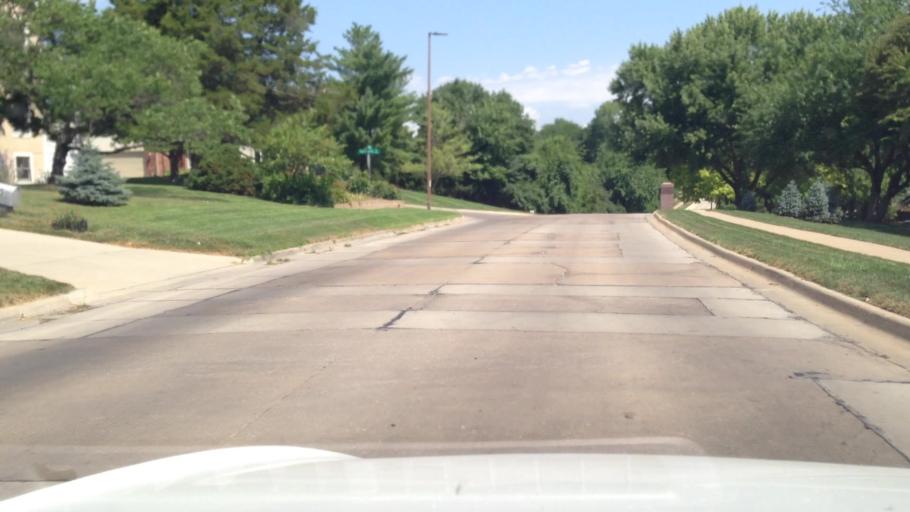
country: US
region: Kansas
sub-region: Douglas County
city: Lawrence
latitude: 38.9457
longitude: -95.2981
